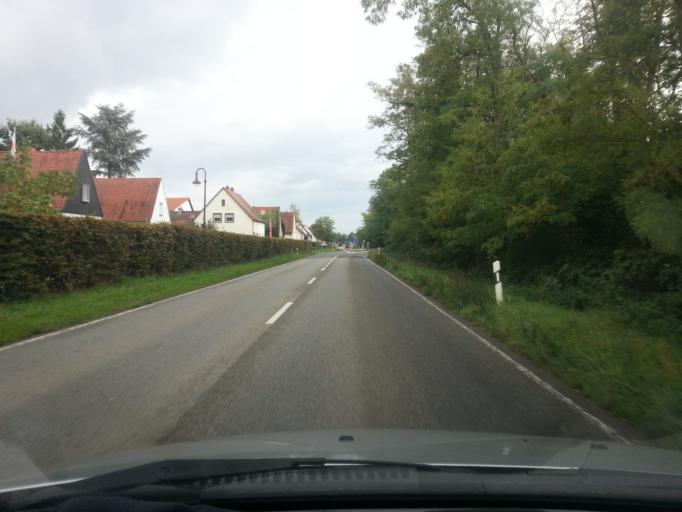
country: DE
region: Rheinland-Pfalz
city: Maxdorf
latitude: 49.4760
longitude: 8.2805
